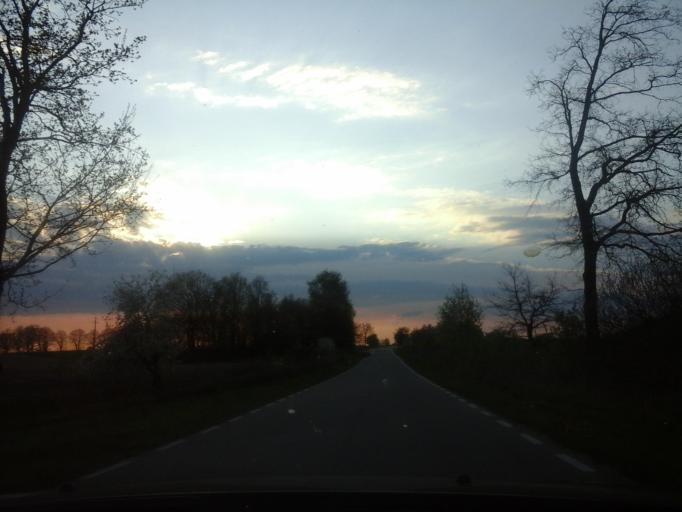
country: PL
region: West Pomeranian Voivodeship
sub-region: Powiat choszczenski
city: Pelczyce
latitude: 53.0098
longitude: 15.3890
